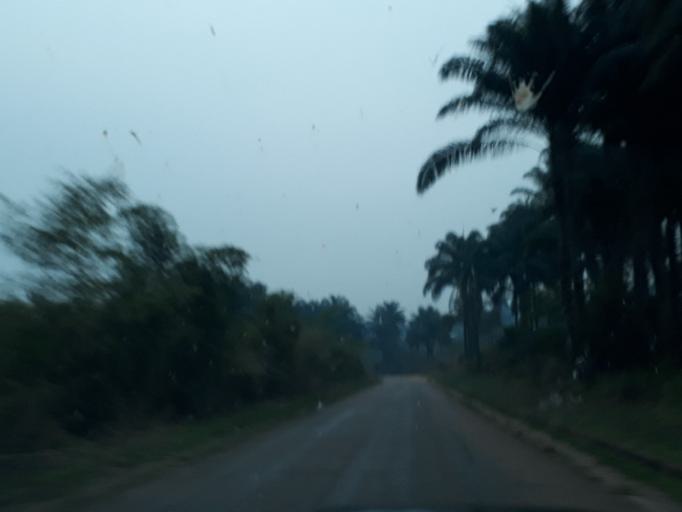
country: CD
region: Bandundu
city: Kikwit
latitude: -5.0744
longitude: 18.8791
